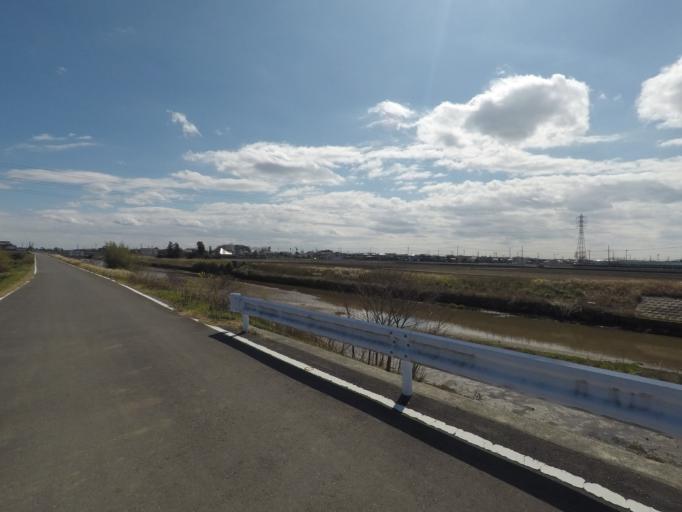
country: JP
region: Ibaraki
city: Moriya
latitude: 35.9634
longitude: 140.0432
